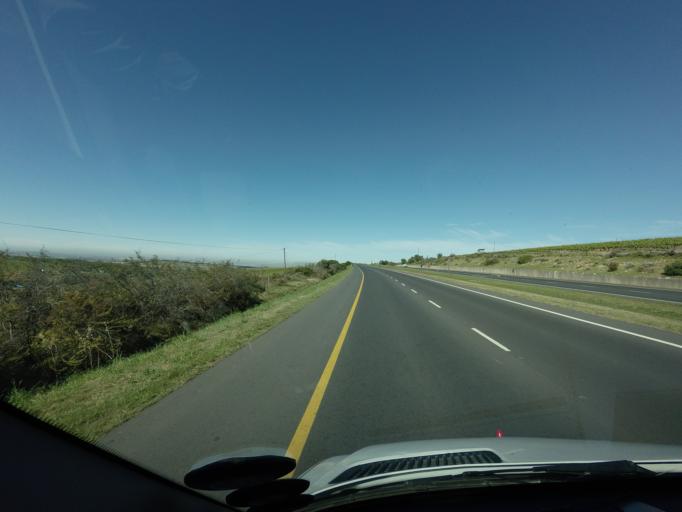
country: ZA
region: Western Cape
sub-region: Cape Winelands District Municipality
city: Stellenbosch
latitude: -33.9622
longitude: 18.7557
